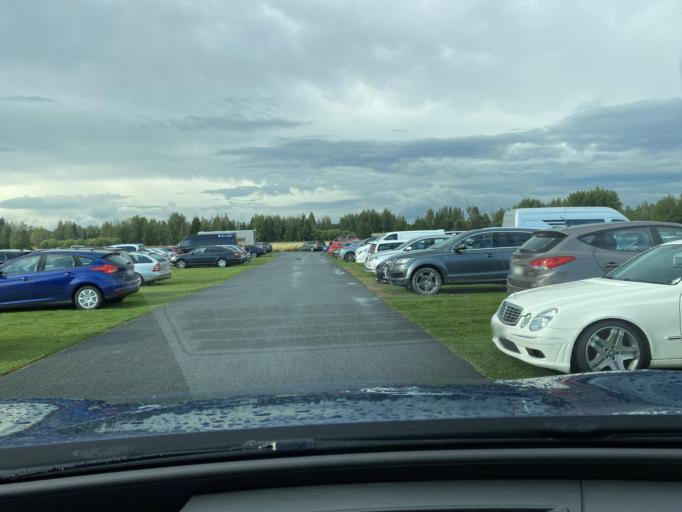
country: FI
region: Southern Ostrobothnia
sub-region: Seinaejoki
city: Alahaermae
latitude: 63.2299
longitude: 22.8499
